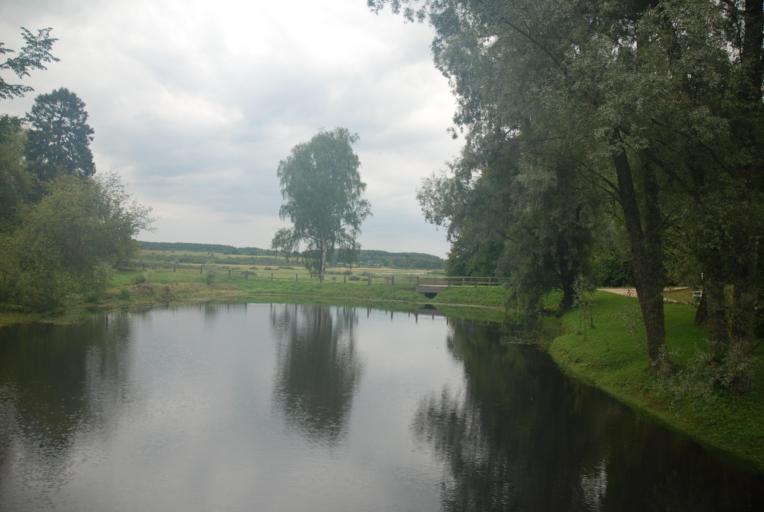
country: RU
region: Pskov
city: Pushkinskiye Gory
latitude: 57.0606
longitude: 28.9224
